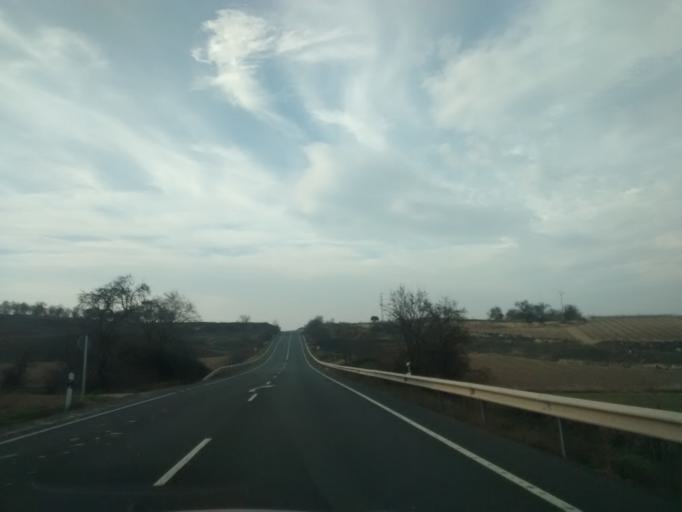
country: ES
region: La Rioja
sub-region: Provincia de La Rioja
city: Briones
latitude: 42.5455
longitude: -2.7953
